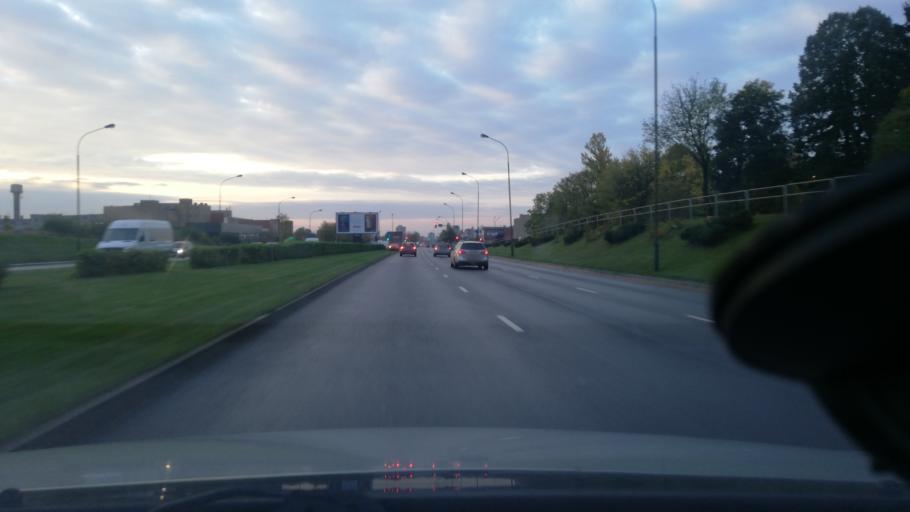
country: LT
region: Klaipedos apskritis
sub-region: Klaipeda
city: Klaipeda
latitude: 55.6876
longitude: 21.1823
